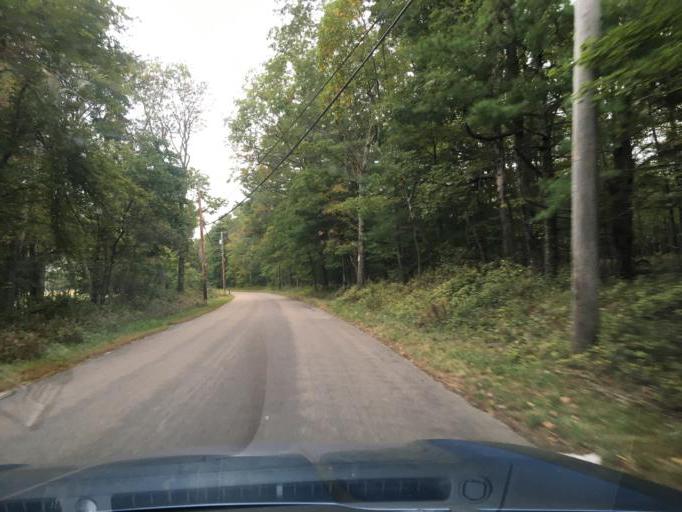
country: US
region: Rhode Island
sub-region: Washington County
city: Exeter
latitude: 41.5886
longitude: -71.5587
